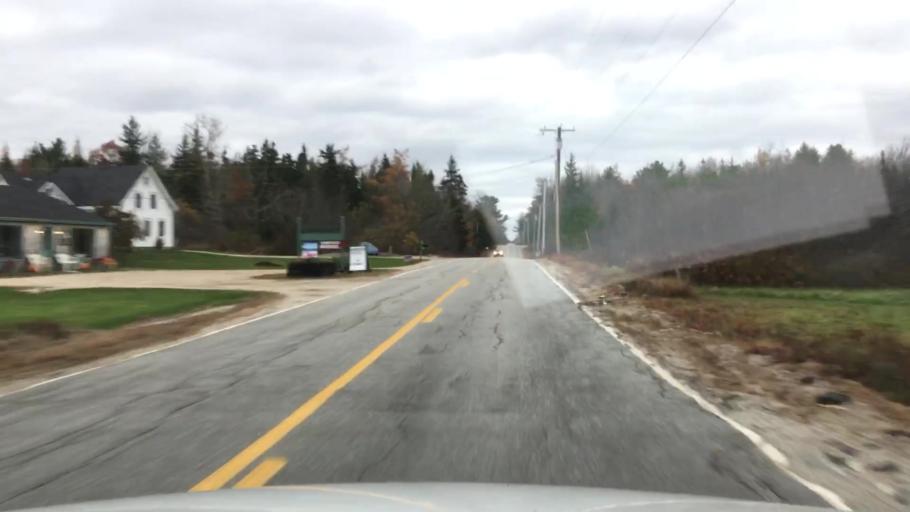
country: US
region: Maine
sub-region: Hancock County
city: Sedgwick
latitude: 44.3365
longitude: -68.5645
